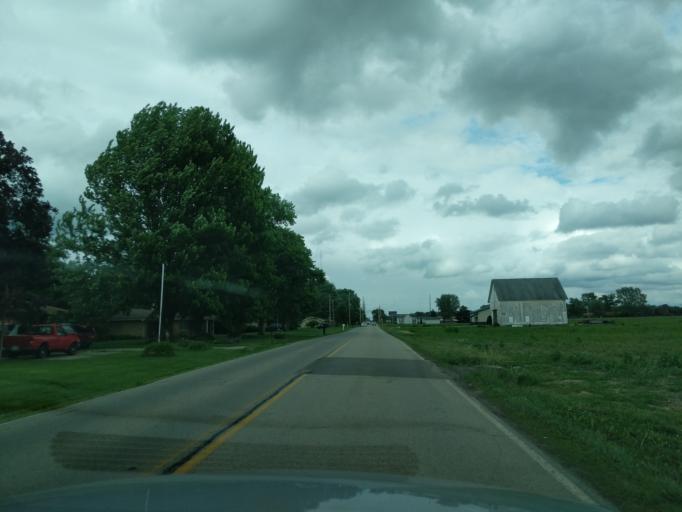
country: US
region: Indiana
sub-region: Madison County
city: Edgewood
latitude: 40.0612
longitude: -85.7228
